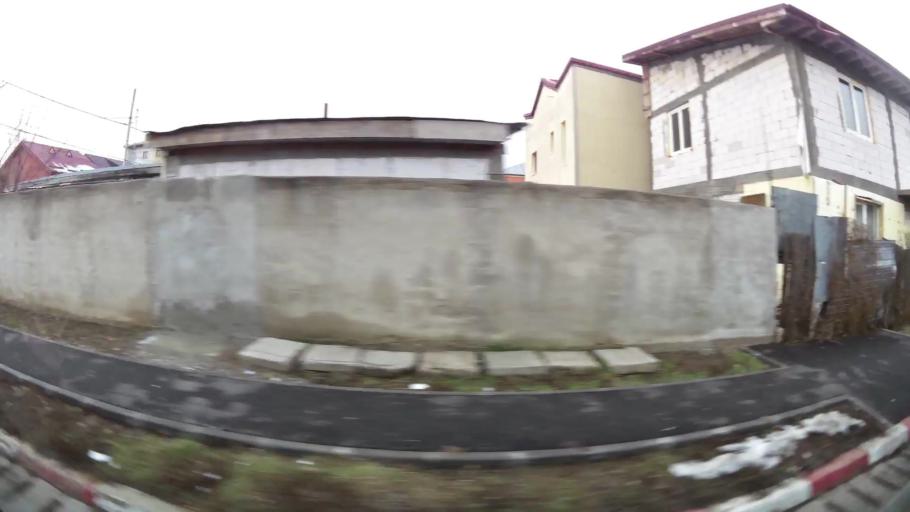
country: RO
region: Ilfov
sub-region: Voluntari City
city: Voluntari
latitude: 44.4834
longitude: 26.1832
